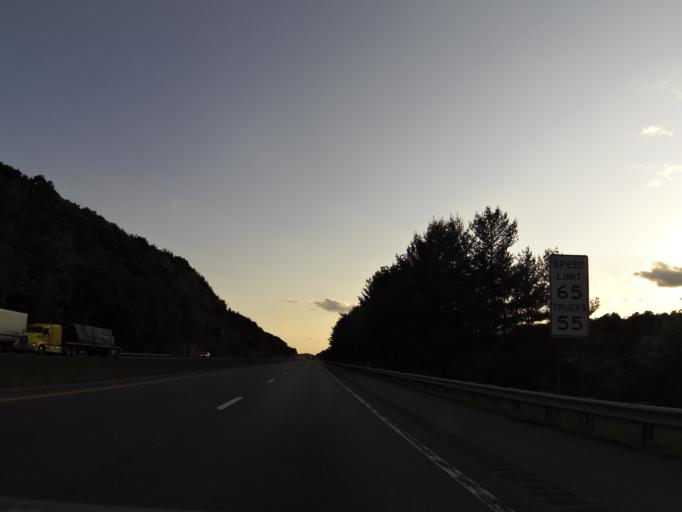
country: US
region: Tennessee
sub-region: Sullivan County
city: Walnut Hill
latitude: 36.5789
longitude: -82.2759
